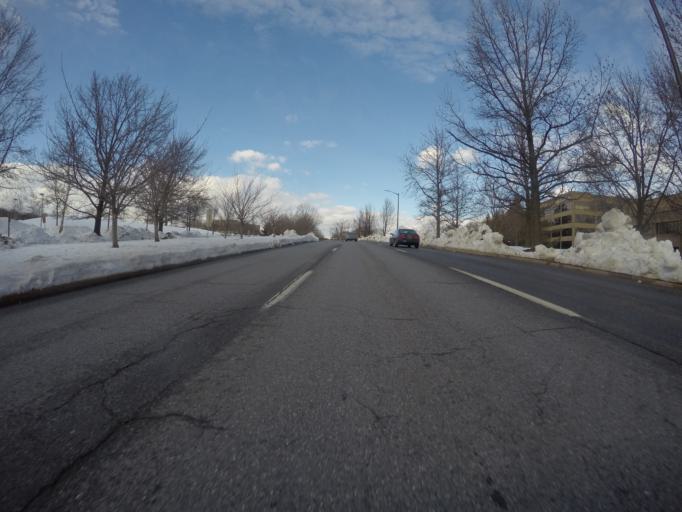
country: US
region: Maryland
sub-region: Howard County
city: Columbia
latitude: 39.2170
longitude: -76.8577
